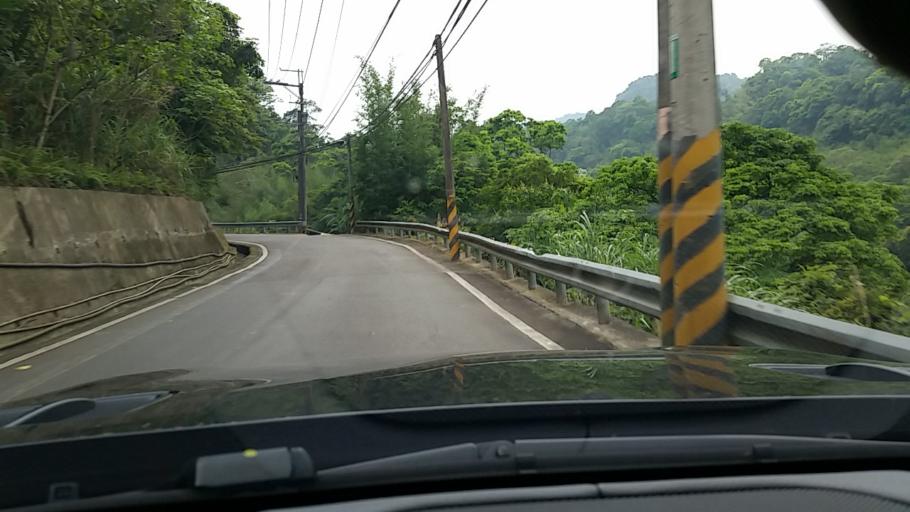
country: TW
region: Taiwan
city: Daxi
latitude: 24.7960
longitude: 121.2813
